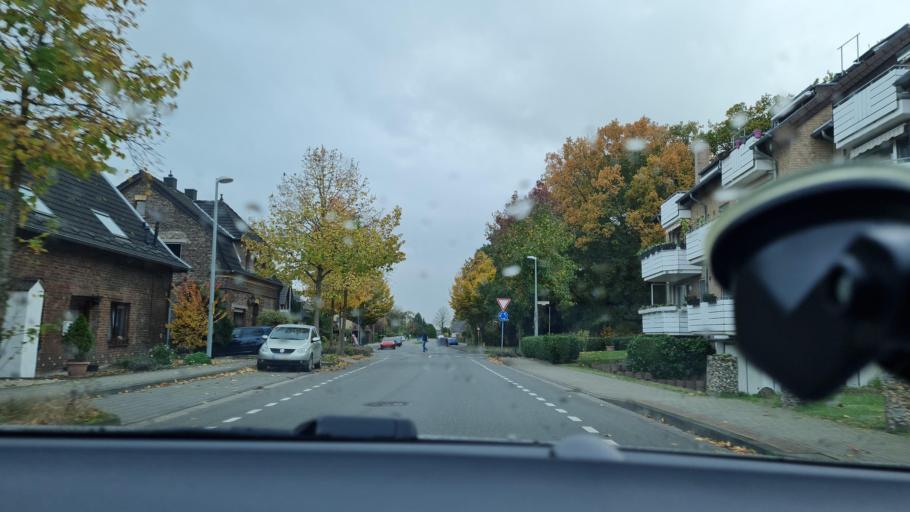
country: DE
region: North Rhine-Westphalia
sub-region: Regierungsbezirk Dusseldorf
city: Wesel
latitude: 51.6063
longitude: 6.6207
